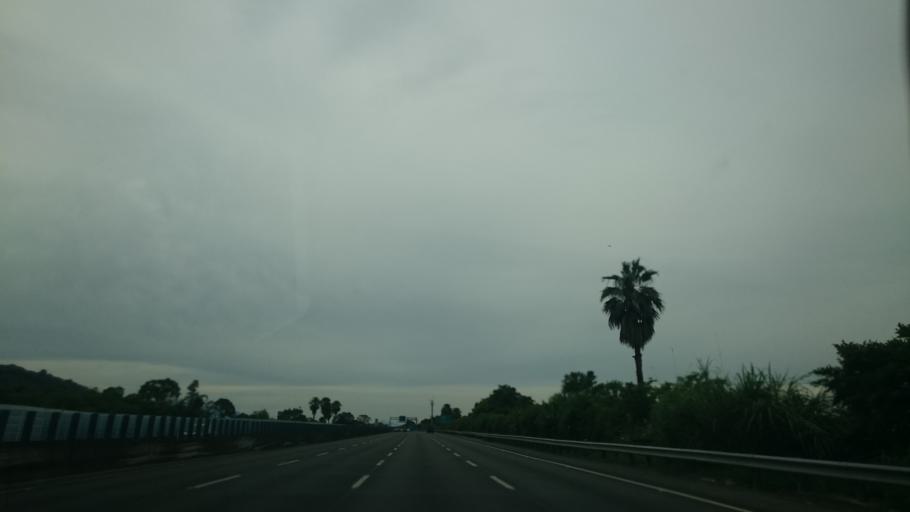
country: TW
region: Taiwan
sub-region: Nantou
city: Nantou
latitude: 23.8677
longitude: 120.7041
